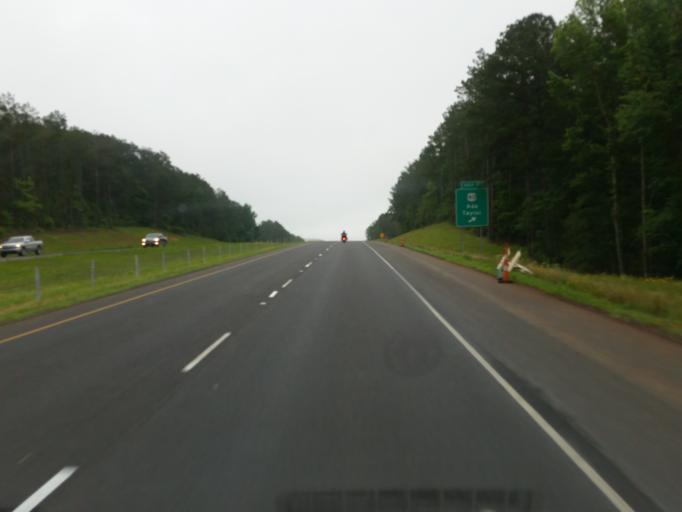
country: US
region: Louisiana
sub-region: Webster Parish
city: Minden
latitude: 32.5640
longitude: -93.1656
